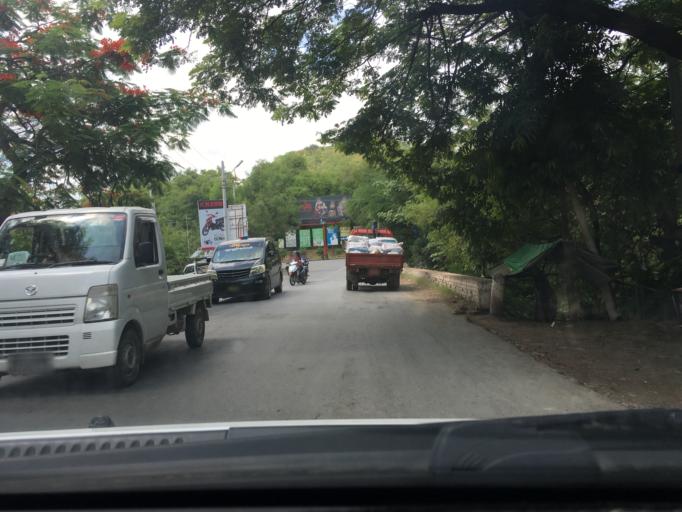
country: MM
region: Mandalay
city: Mandalay
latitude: 22.0222
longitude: 96.1082
